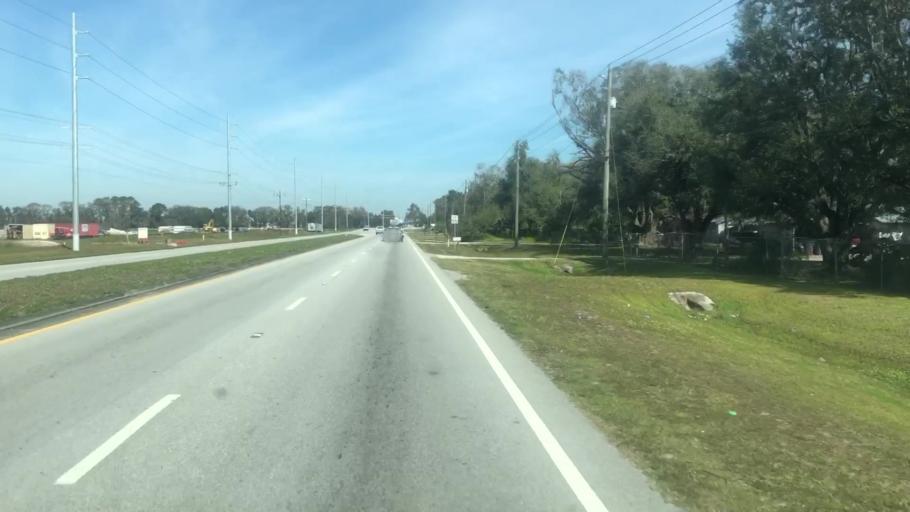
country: US
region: Florida
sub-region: Polk County
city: Winston
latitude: 27.9983
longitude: -82.0558
